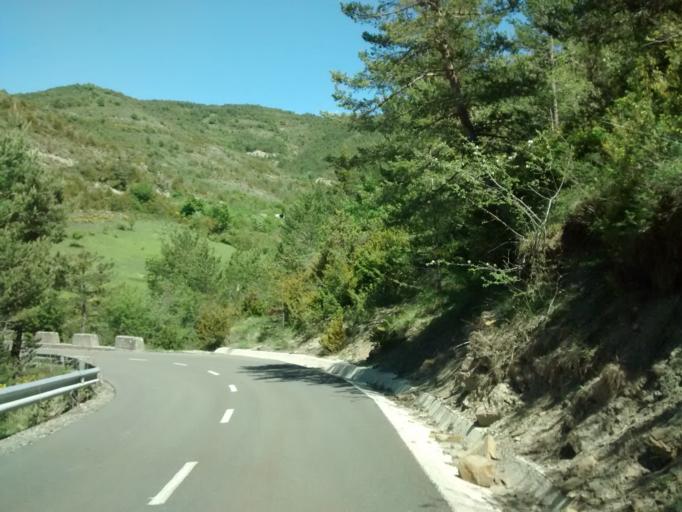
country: ES
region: Aragon
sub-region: Provincia de Huesca
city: Borau
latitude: 42.6772
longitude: -0.6162
